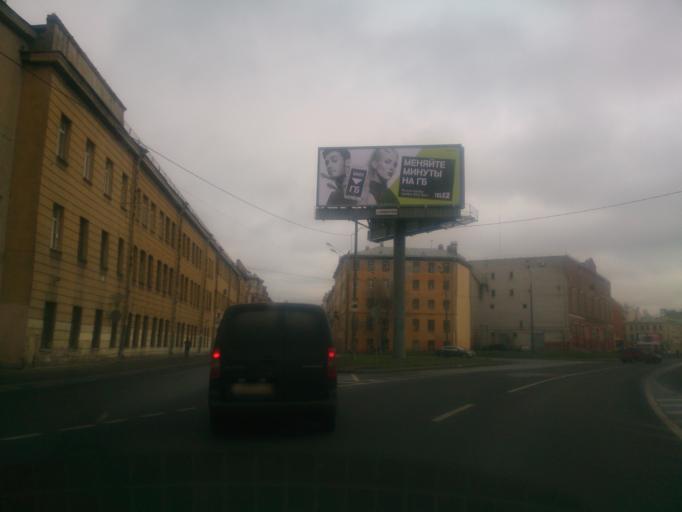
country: RU
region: St.-Petersburg
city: Centralniy
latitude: 59.9163
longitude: 30.3407
